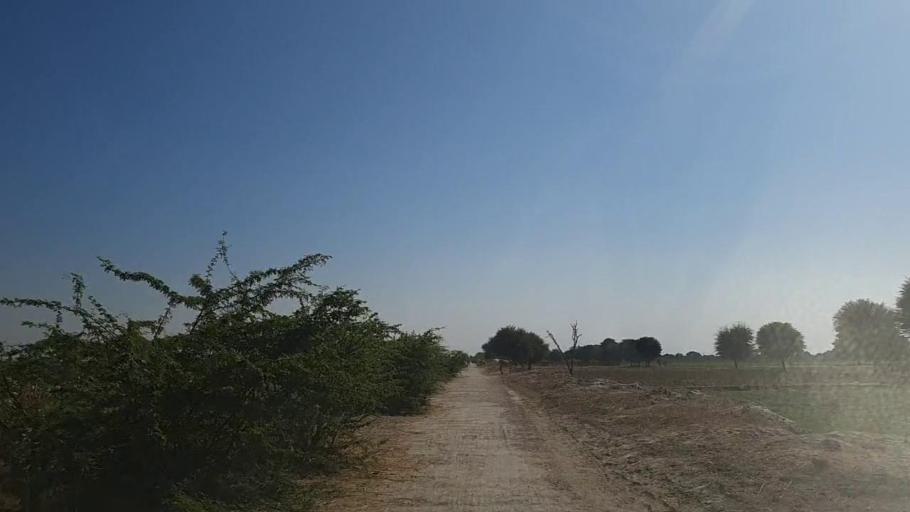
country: PK
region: Sindh
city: Samaro
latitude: 25.2410
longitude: 69.4838
